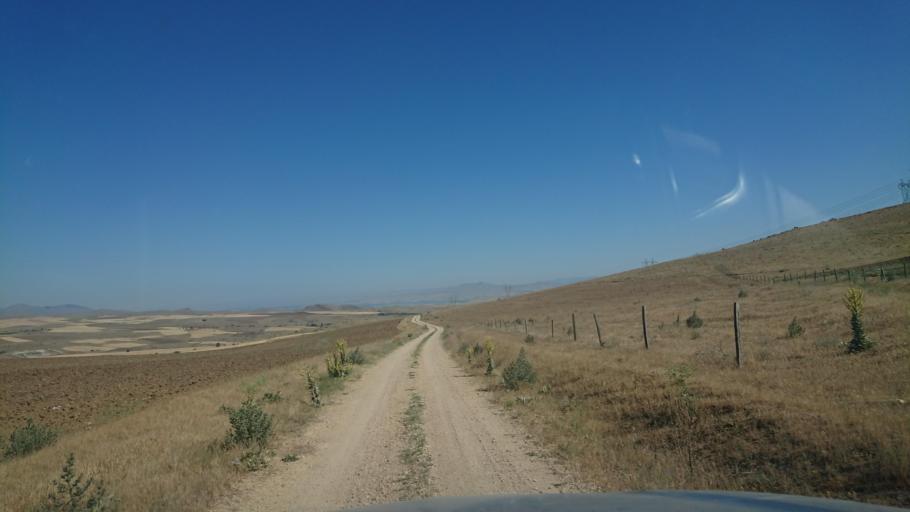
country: TR
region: Aksaray
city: Agacoren
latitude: 38.9147
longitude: 33.8940
